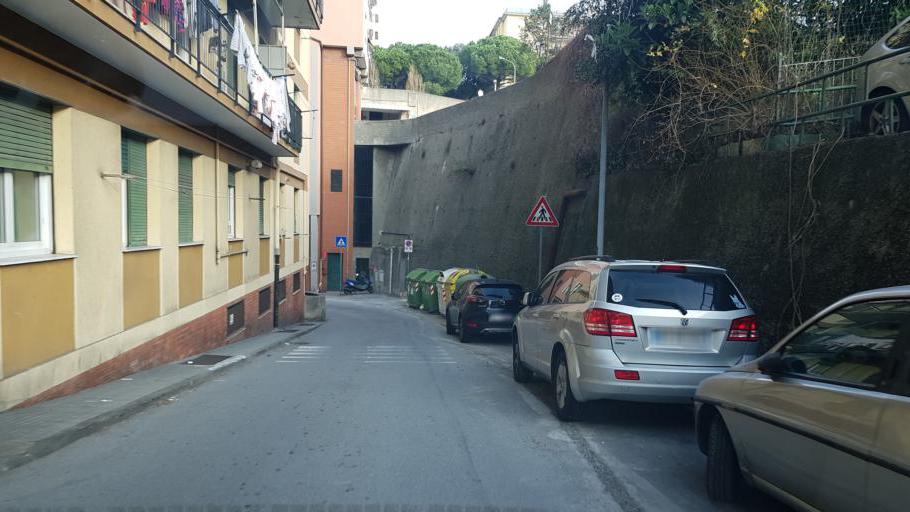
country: IT
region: Liguria
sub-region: Provincia di Genova
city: San Teodoro
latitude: 44.4149
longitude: 8.8995
